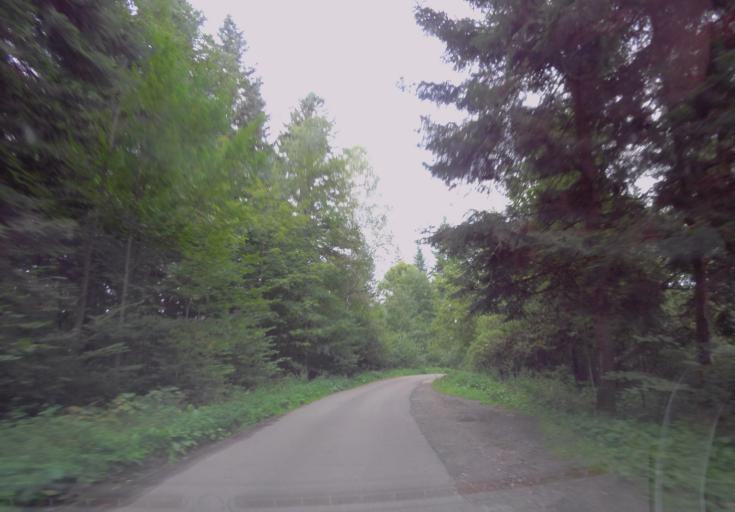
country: PL
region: Subcarpathian Voivodeship
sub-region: Powiat leski
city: Polanczyk
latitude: 49.3041
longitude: 22.5102
